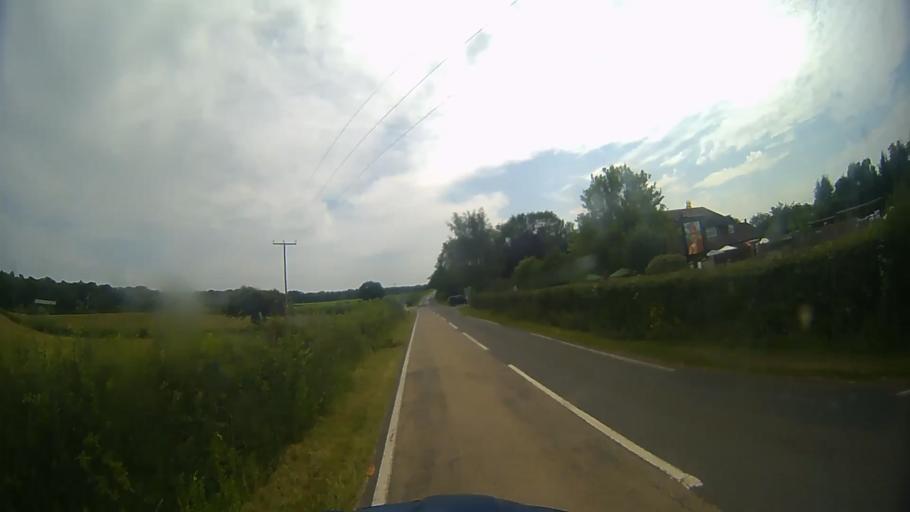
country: GB
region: England
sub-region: Hampshire
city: Kingsley
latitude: 51.1681
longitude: -0.8598
